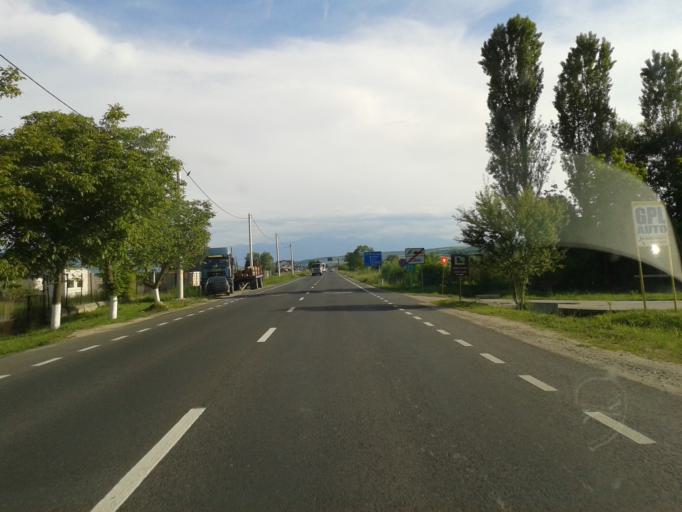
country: RO
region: Hunedoara
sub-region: Comuna Calan
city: Calan
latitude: 45.7310
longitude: 22.9966
